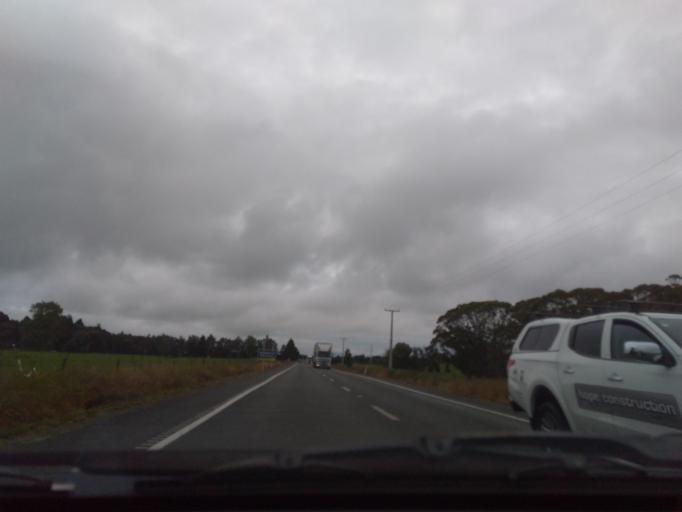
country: NZ
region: Northland
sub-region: Whangarei
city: Ruakaka
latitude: -35.9996
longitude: 174.4166
